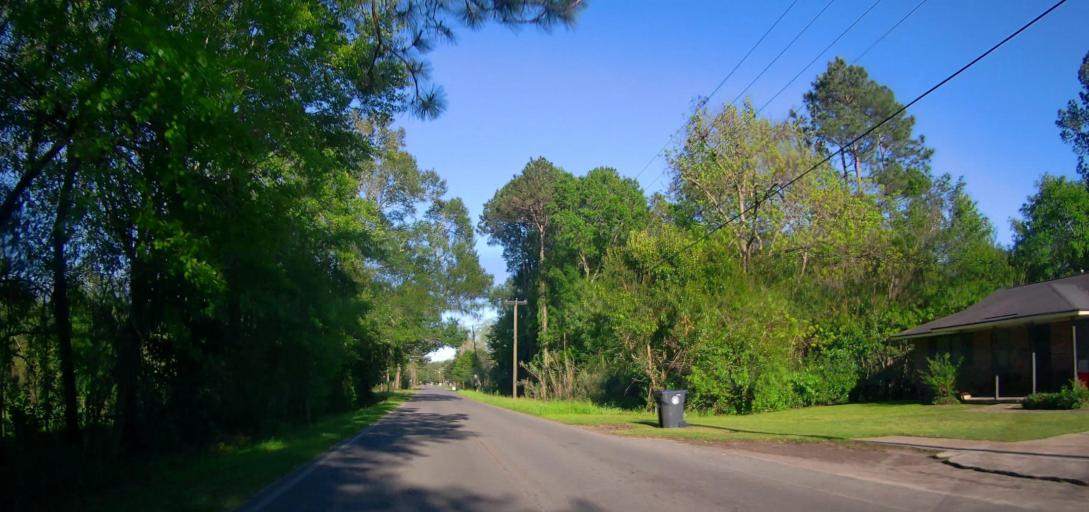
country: US
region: Georgia
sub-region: Ben Hill County
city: Fitzgerald
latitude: 31.7240
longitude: -83.2474
